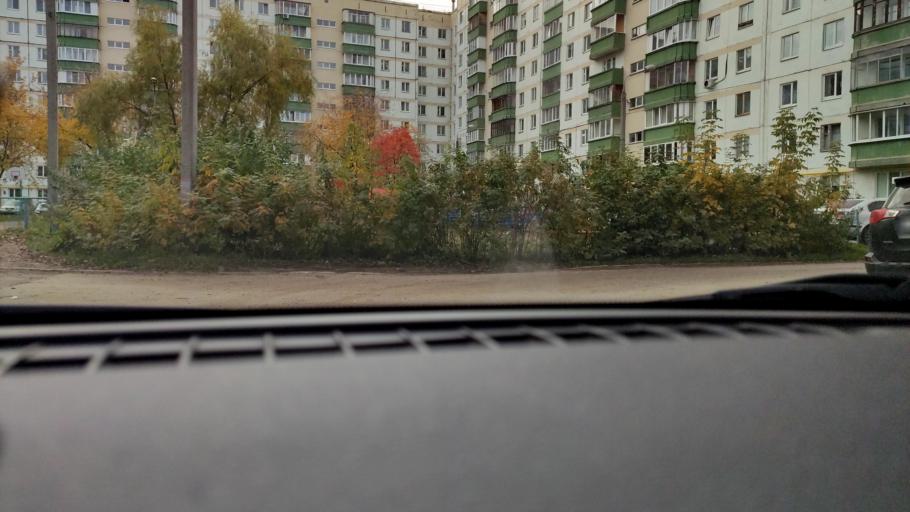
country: RU
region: Perm
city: Perm
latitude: 57.9732
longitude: 56.2001
